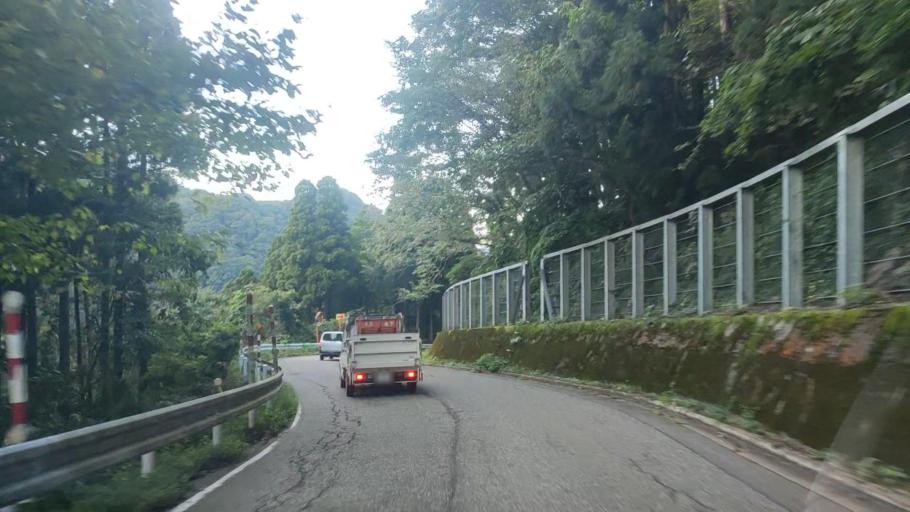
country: JP
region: Toyama
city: Nanto-shi
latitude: 36.5447
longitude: 137.0063
